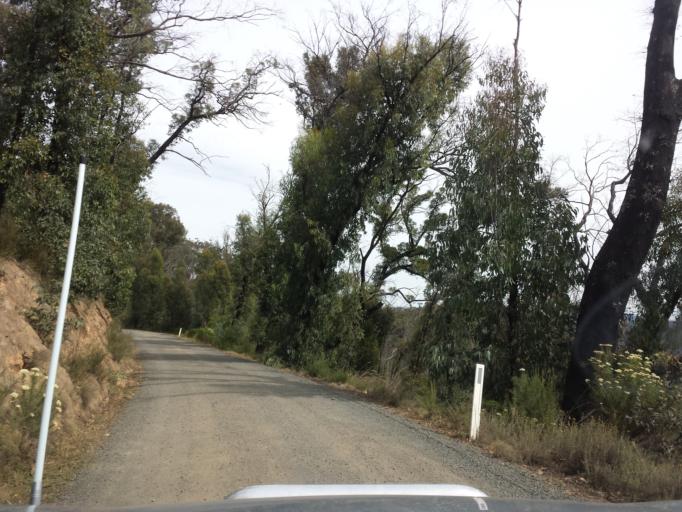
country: AU
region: Victoria
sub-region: Latrobe
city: Moe
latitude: -37.8131
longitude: 146.4007
